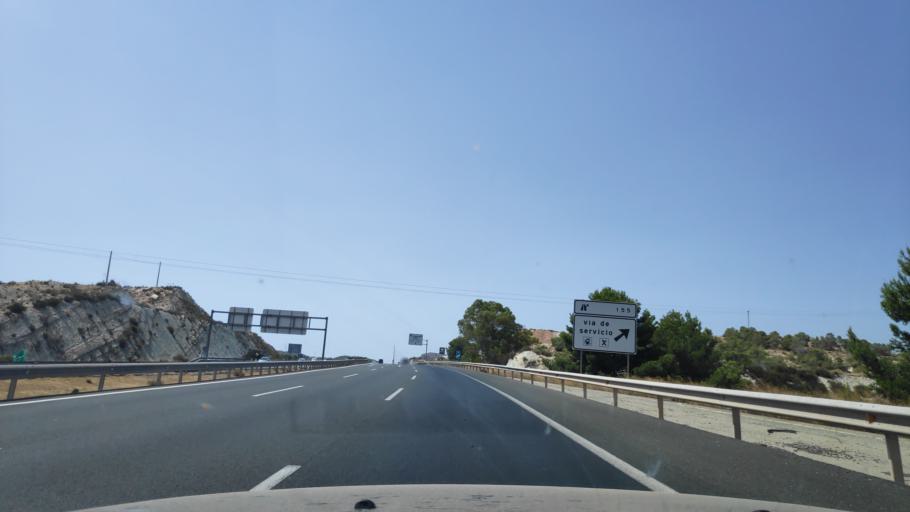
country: ES
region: Murcia
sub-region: Murcia
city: Murcia
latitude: 37.8798
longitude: -1.1315
